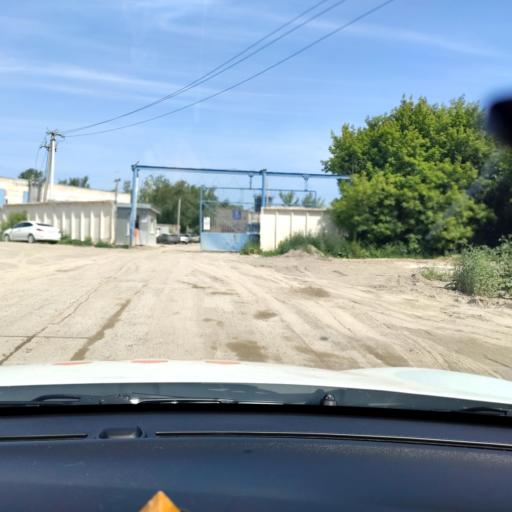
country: RU
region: Tatarstan
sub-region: Gorod Kazan'
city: Kazan
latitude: 55.7324
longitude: 49.0929
